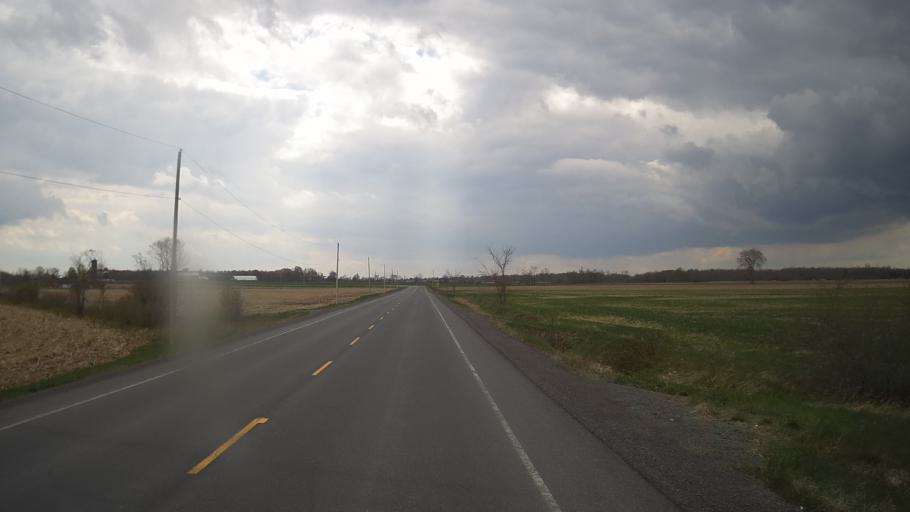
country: CA
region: Ontario
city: Hawkesbury
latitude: 45.5552
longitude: -74.5400
